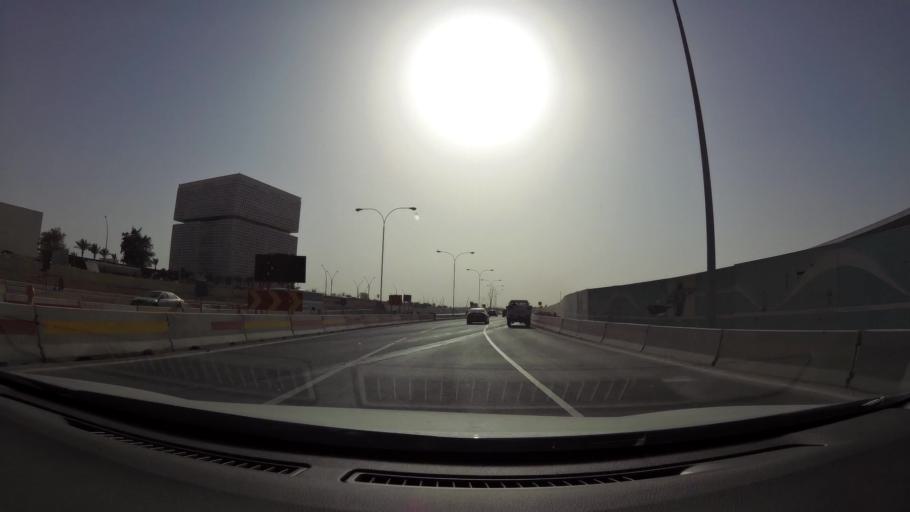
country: QA
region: Baladiyat ar Rayyan
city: Ar Rayyan
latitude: 25.3199
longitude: 51.4380
